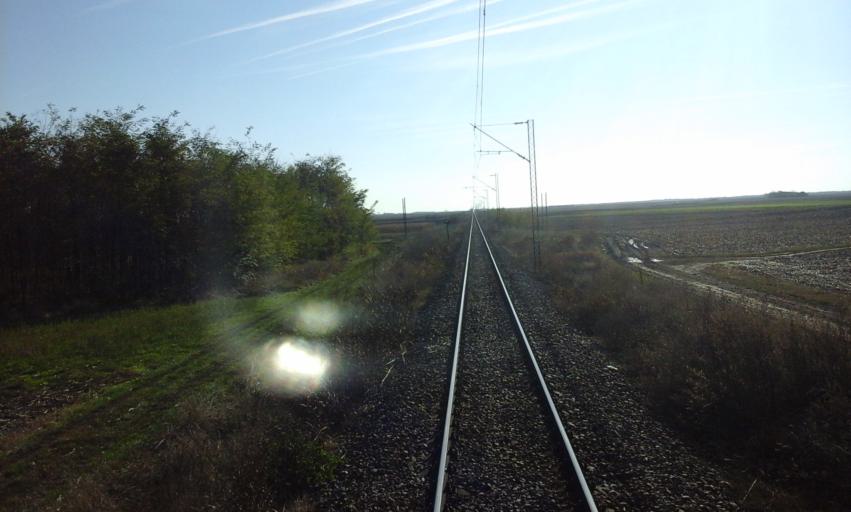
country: RS
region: Autonomna Pokrajina Vojvodina
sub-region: Severnobacki Okrug
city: Backa Topola
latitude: 45.9281
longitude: 19.6665
